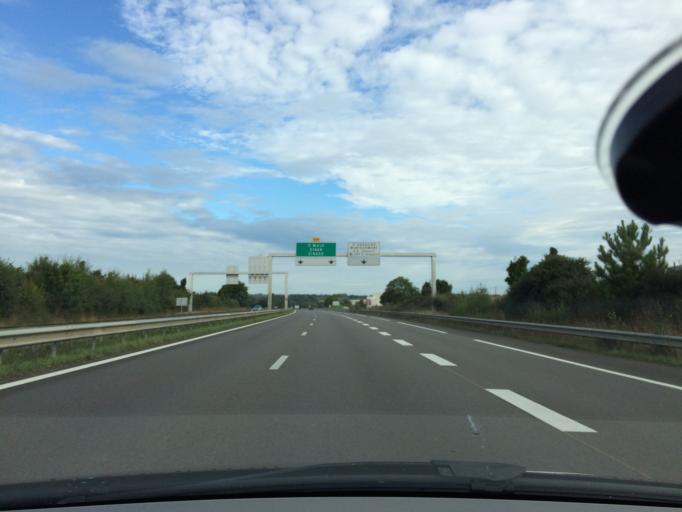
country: FR
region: Brittany
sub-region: Departement d'Ille-et-Vilaine
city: Saint-Gregoire
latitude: 48.1484
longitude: -1.6990
